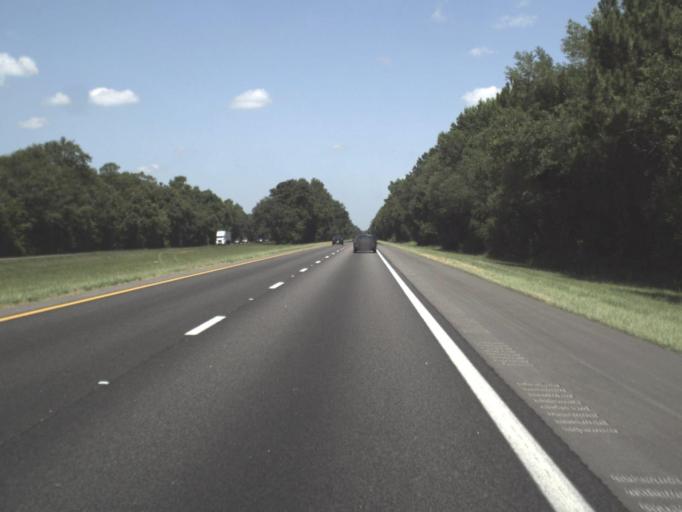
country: US
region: Florida
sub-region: Madison County
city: Madison
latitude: 30.4051
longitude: -83.3971
